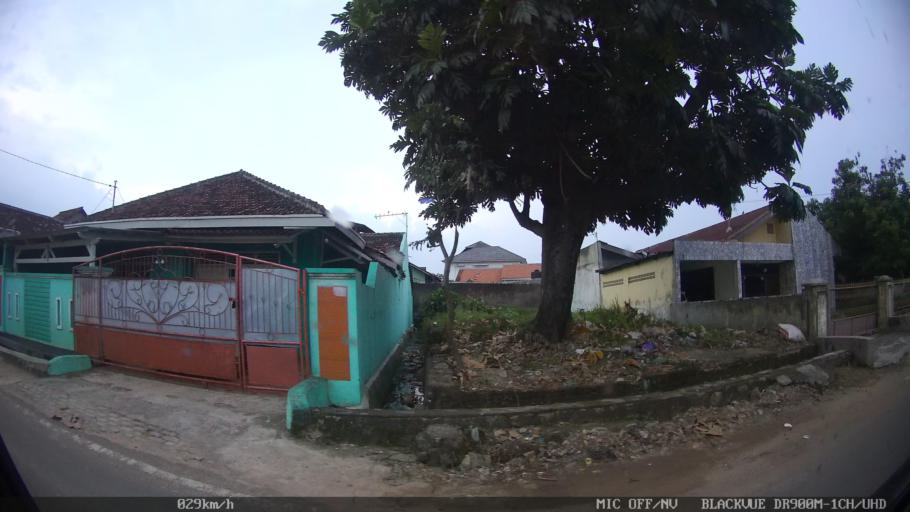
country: ID
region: Lampung
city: Kedaton
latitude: -5.3991
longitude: 105.2661
